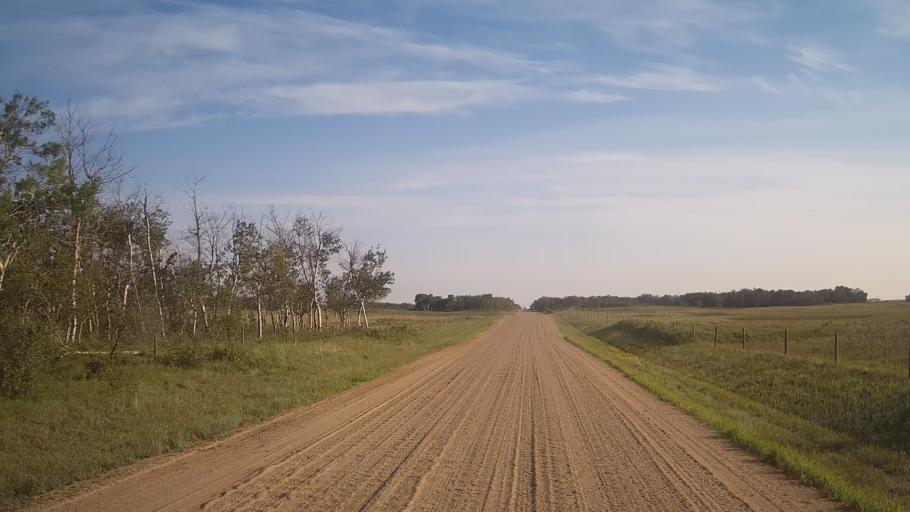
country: CA
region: Saskatchewan
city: Saskatoon
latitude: 51.8333
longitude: -106.5239
